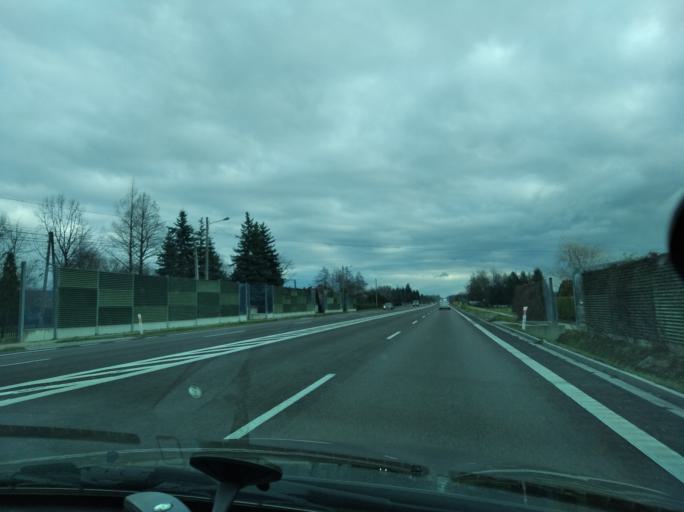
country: PL
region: Subcarpathian Voivodeship
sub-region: Powiat lancucki
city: Kraczkowa
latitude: 50.0447
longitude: 22.1361
